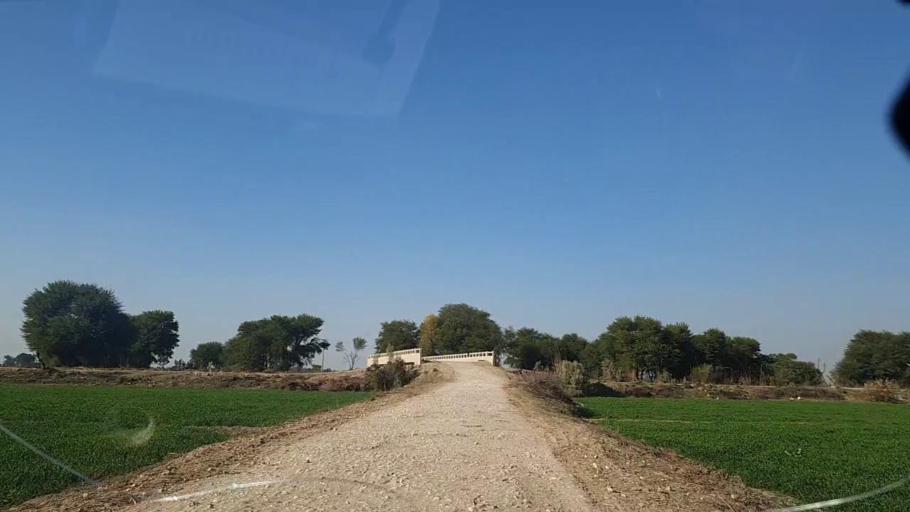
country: PK
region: Sindh
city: Khanpur
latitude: 27.7893
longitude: 69.3511
